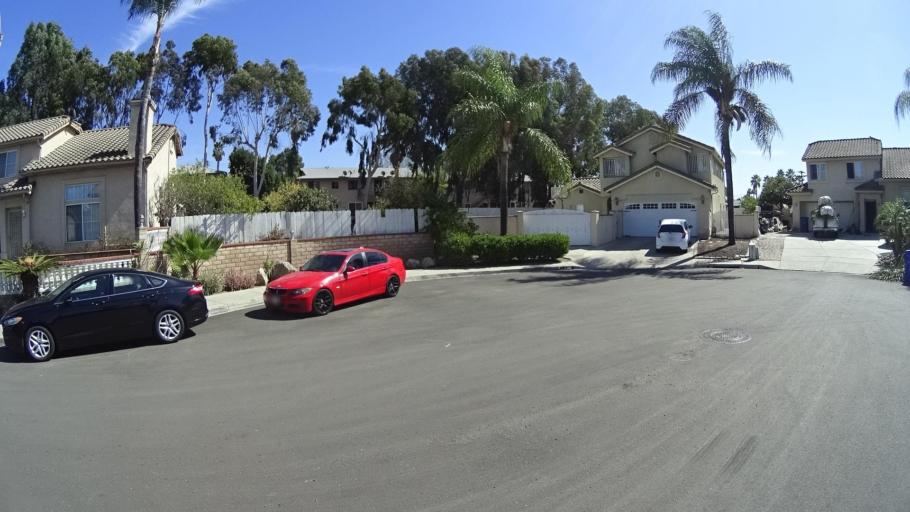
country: US
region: California
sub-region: San Diego County
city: La Presa
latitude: 32.7101
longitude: -117.0086
